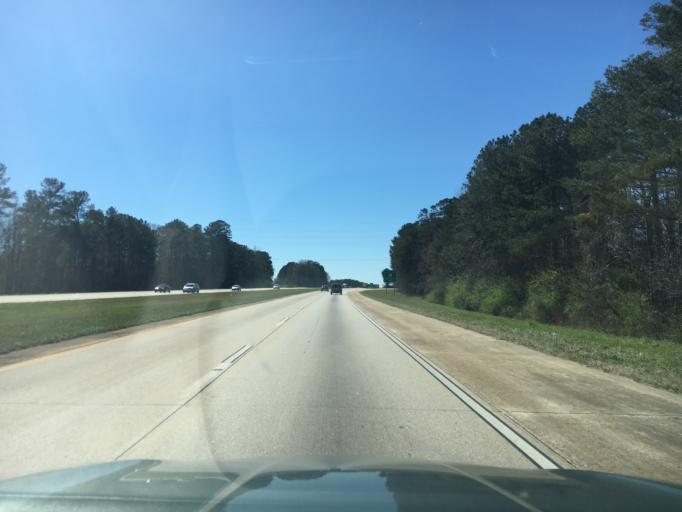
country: US
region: Georgia
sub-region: Troup County
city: La Grange
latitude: 33.0047
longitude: -85.0057
